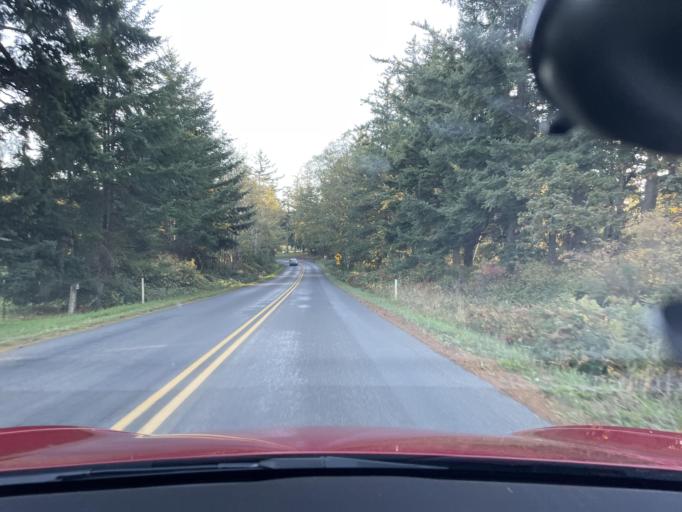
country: US
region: Washington
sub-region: San Juan County
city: Friday Harbor
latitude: 48.5632
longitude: -123.1539
